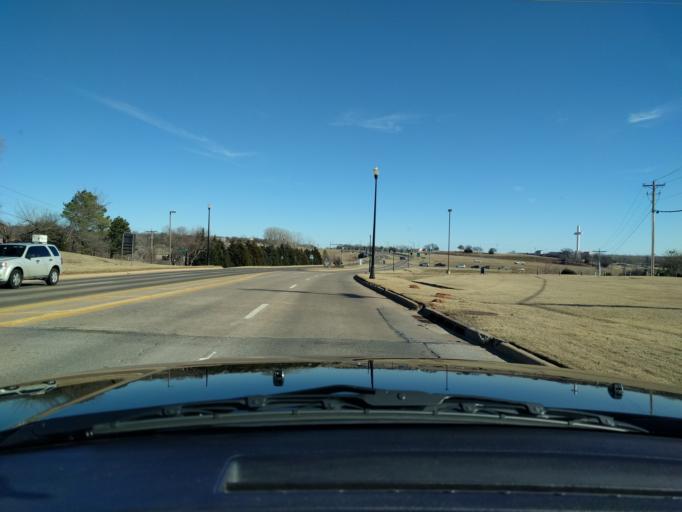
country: US
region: Oklahoma
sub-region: Oklahoma County
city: Edmond
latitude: 35.6527
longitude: -97.4294
